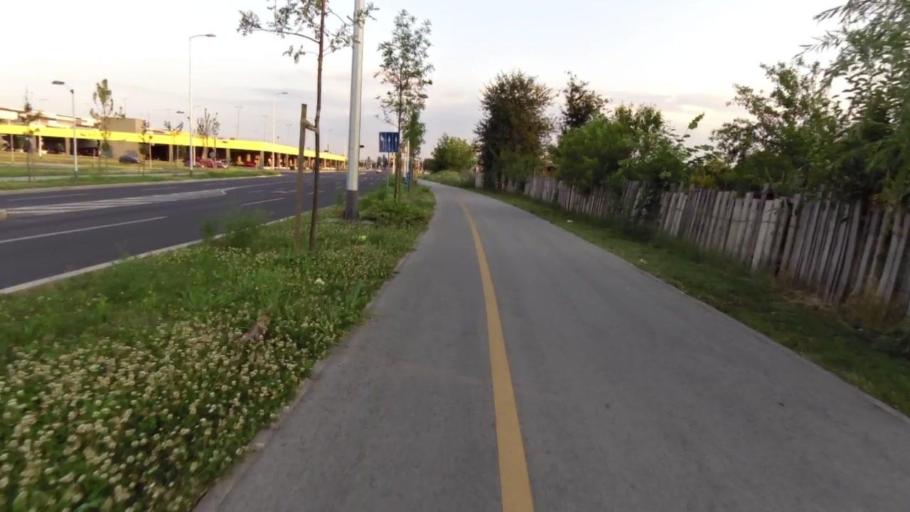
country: HR
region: Grad Zagreb
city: Dubrava
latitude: 45.8045
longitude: 16.0481
